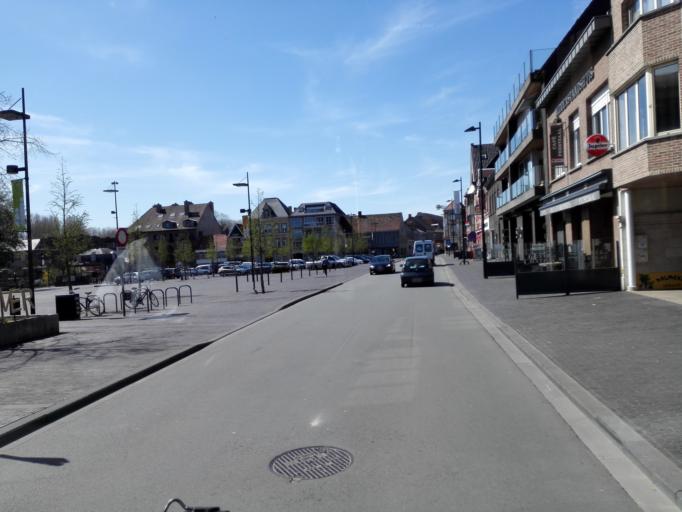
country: BE
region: Flanders
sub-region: Provincie West-Vlaanderen
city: Ingelmunster
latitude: 50.9204
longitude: 3.2551
